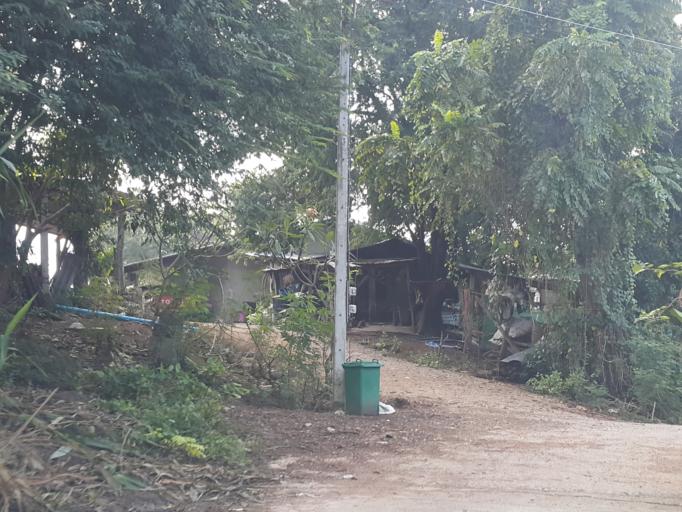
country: TH
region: Lampang
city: Mae Mo
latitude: 18.2448
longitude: 99.5882
